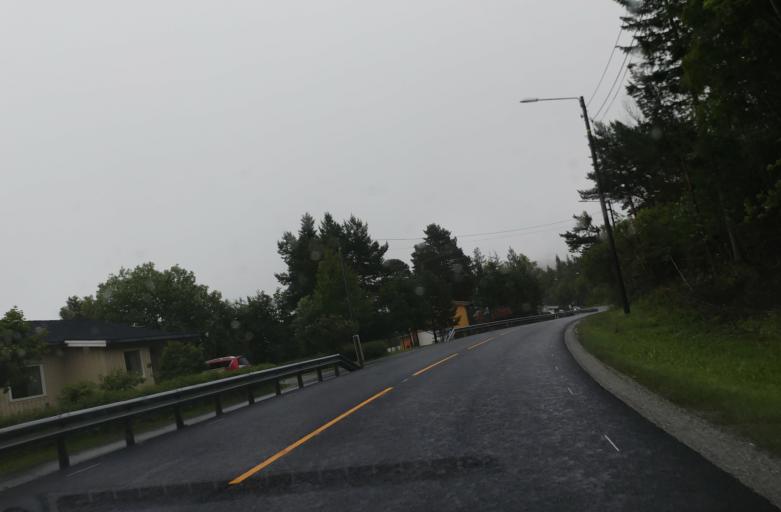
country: NO
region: Nord-Trondelag
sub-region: Stjordal
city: Stjordal
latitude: 63.4428
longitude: 10.8702
